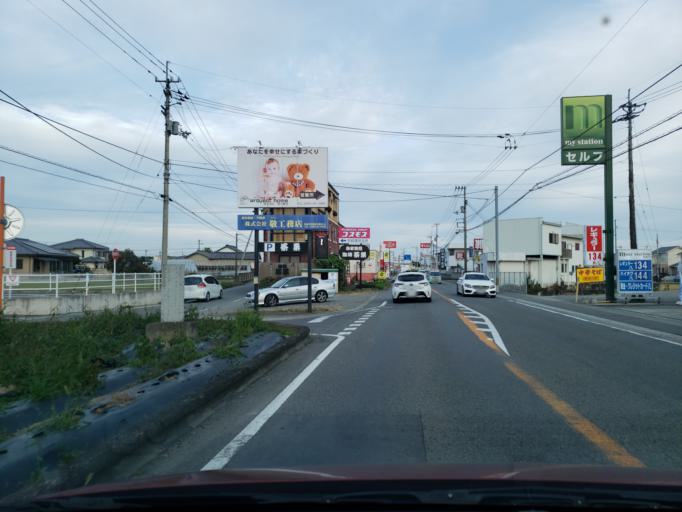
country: JP
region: Tokushima
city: Kamojimacho-jogejima
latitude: 34.0841
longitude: 134.2787
